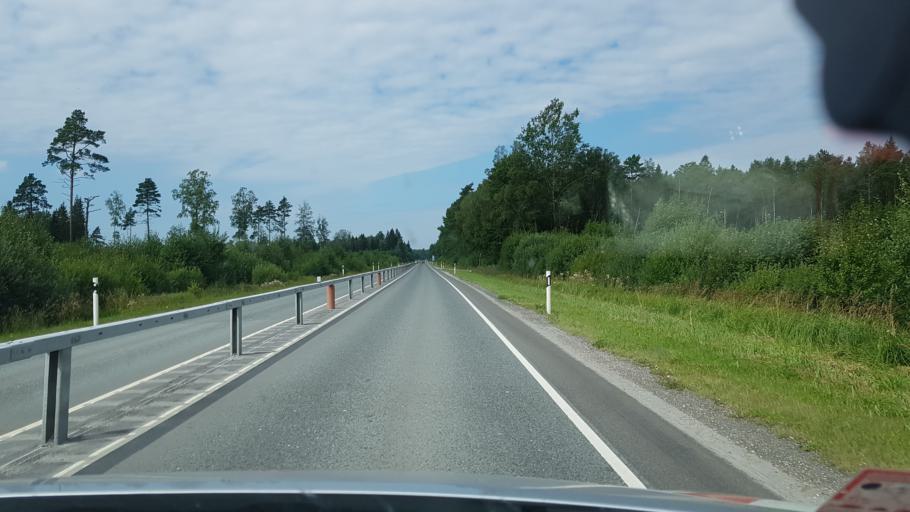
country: EE
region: Raplamaa
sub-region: Kohila vald
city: Kohila
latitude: 59.2344
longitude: 24.7690
